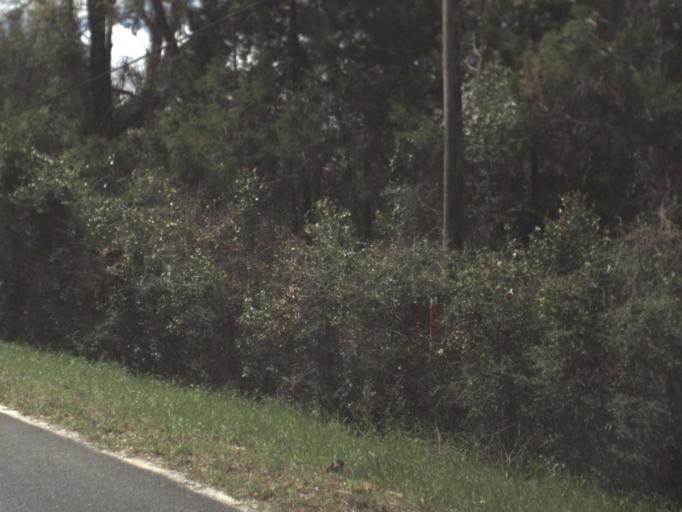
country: US
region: Florida
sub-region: Wakulla County
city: Crawfordville
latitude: 30.1518
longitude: -84.3843
